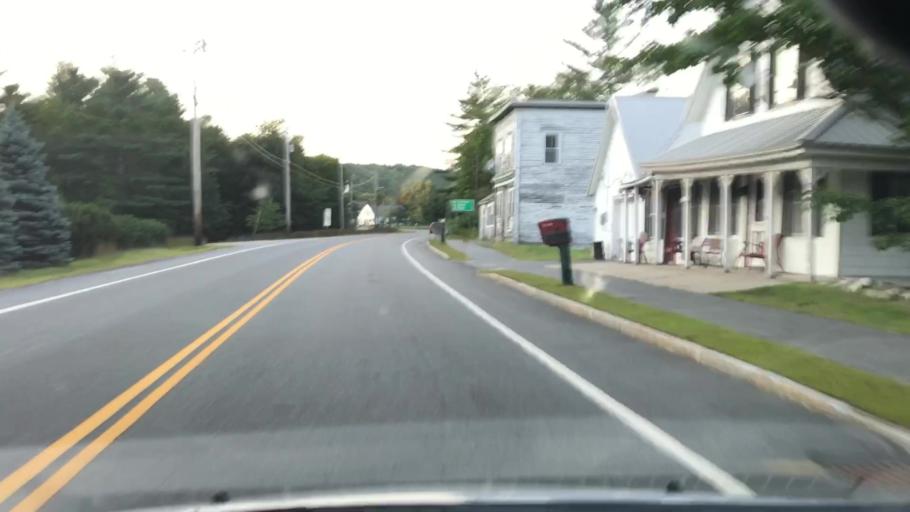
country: US
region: New Hampshire
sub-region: Grafton County
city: Rumney
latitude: 43.9204
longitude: -71.8894
